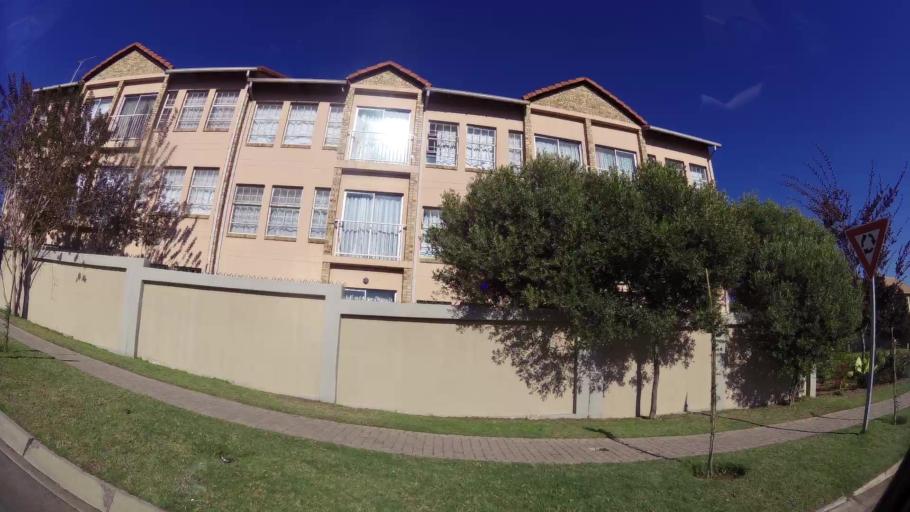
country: ZA
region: Gauteng
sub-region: City of Johannesburg Metropolitan Municipality
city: Midrand
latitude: -25.9171
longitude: 28.1292
